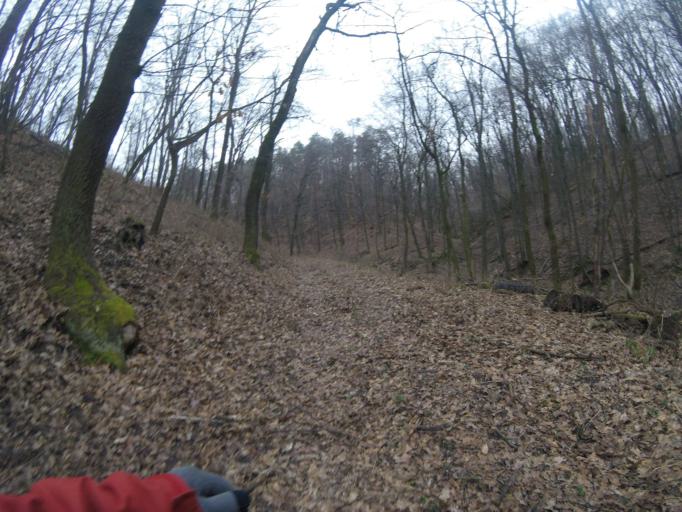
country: HU
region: Baranya
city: Mecseknadasd
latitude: 46.1409
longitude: 18.5183
